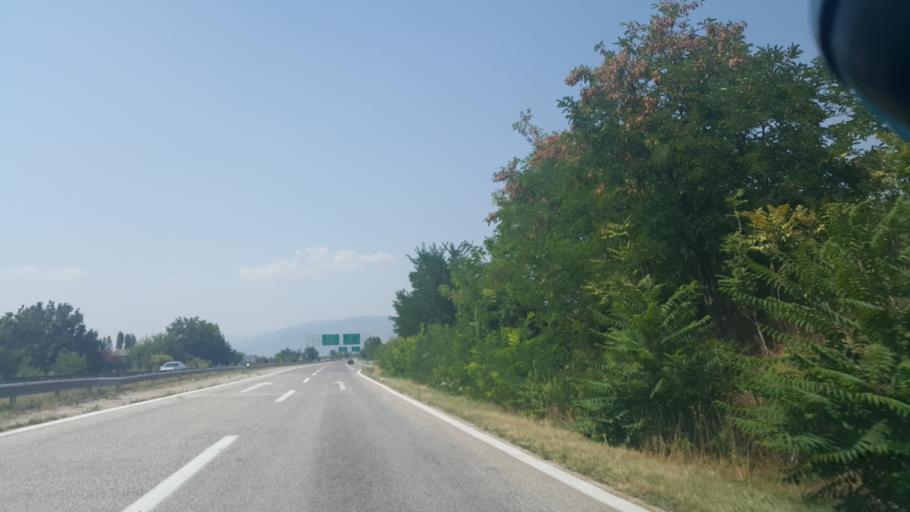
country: MK
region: Petrovec
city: Petrovec
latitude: 41.9291
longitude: 21.6303
